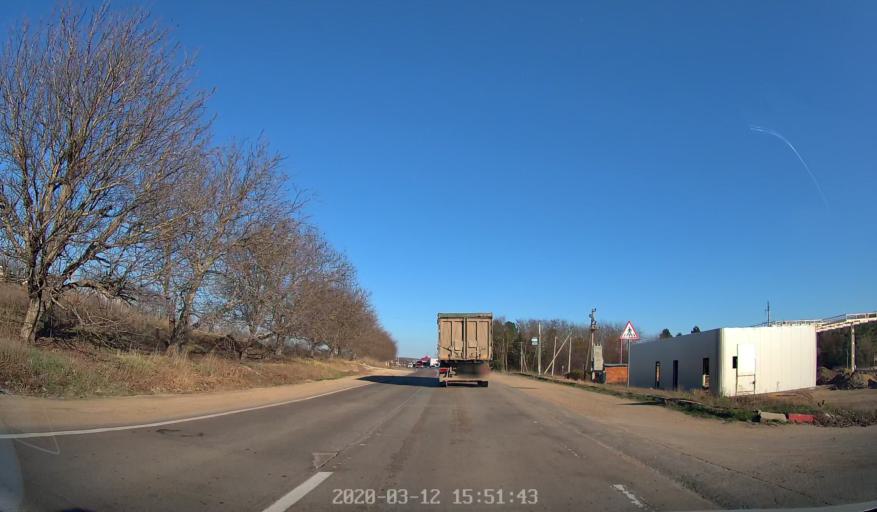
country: MD
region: Chisinau
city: Ciorescu
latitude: 47.0666
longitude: 28.9721
